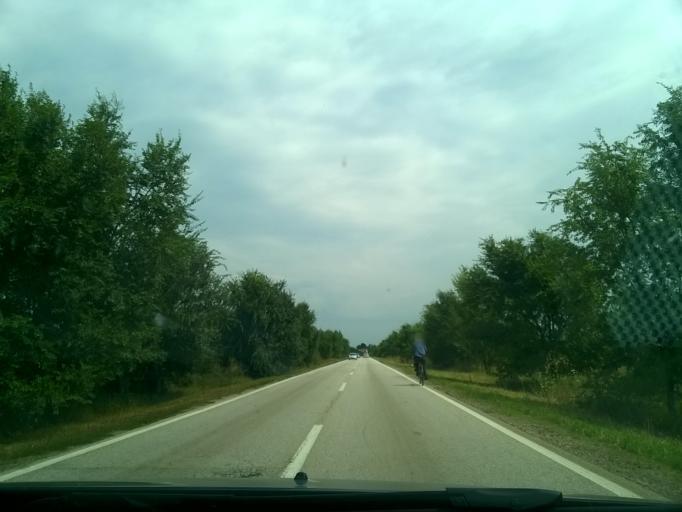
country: RS
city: Sutjeska
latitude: 45.3796
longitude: 20.6832
